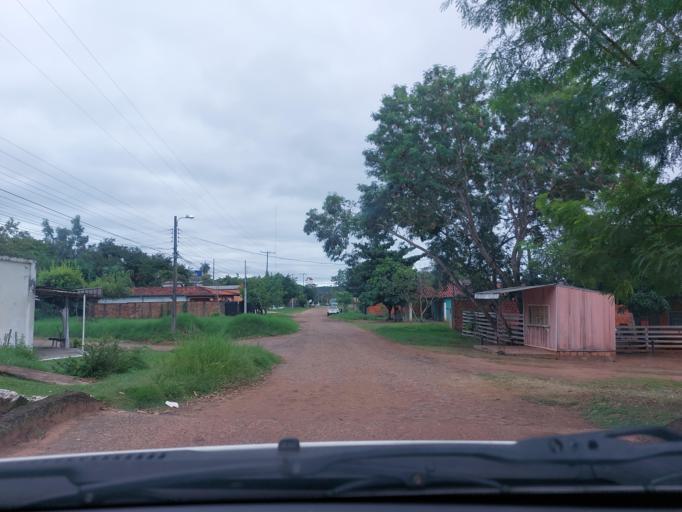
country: PY
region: San Pedro
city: Guayaybi
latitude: -24.6655
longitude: -56.4360
